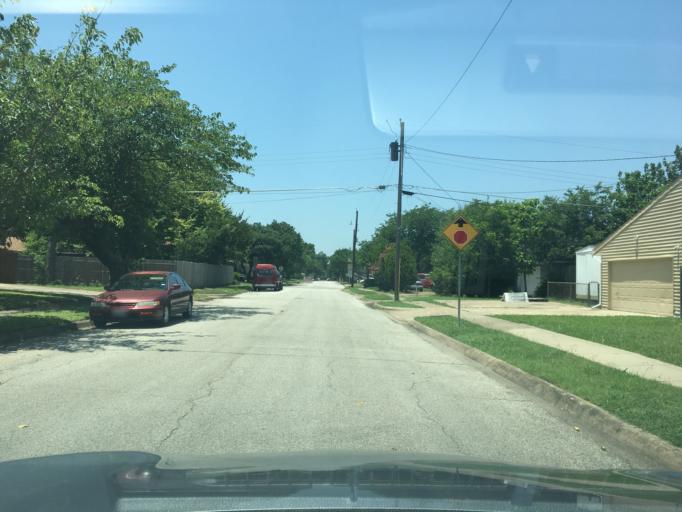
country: US
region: Texas
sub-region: Dallas County
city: Garland
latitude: 32.9134
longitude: -96.6890
